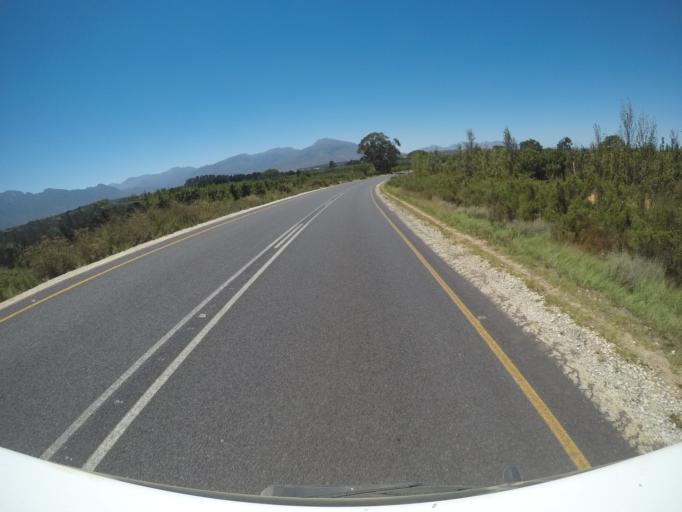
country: ZA
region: Western Cape
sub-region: Overberg District Municipality
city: Grabouw
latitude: -34.0594
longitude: 19.1373
